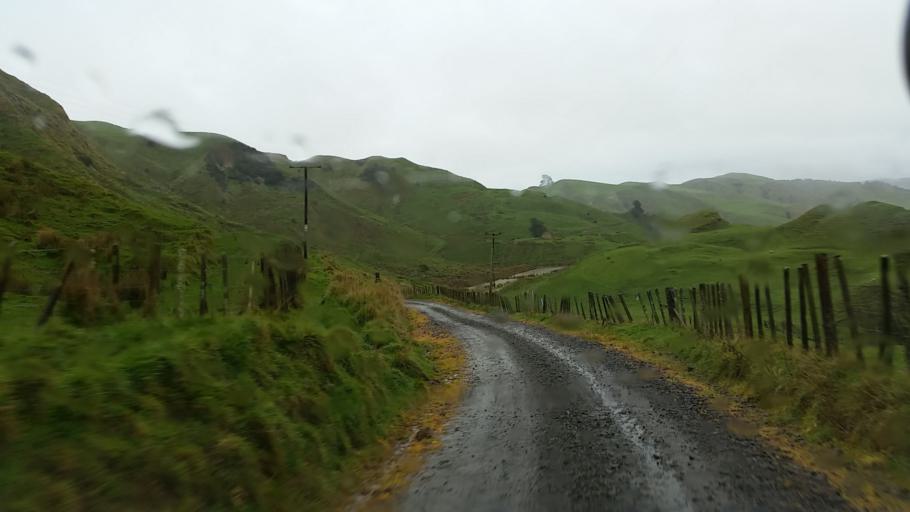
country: NZ
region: Taranaki
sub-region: South Taranaki District
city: Eltham
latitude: -39.4741
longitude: 174.4148
